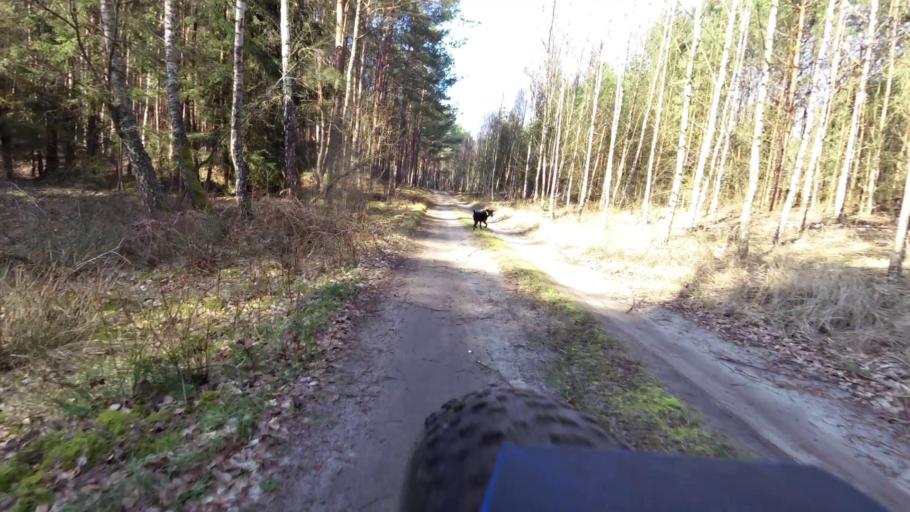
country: PL
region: Lubusz
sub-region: Powiat sulecinski
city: Torzym
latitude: 52.2214
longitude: 14.9794
